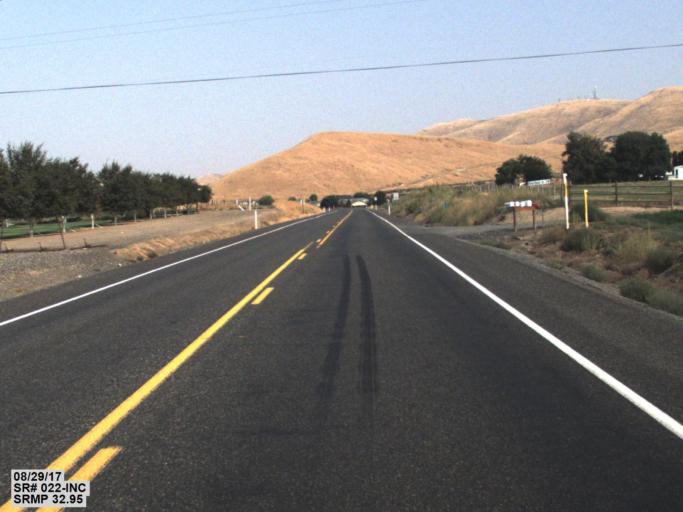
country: US
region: Washington
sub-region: Benton County
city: Prosser
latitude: 46.1931
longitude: -119.8013
